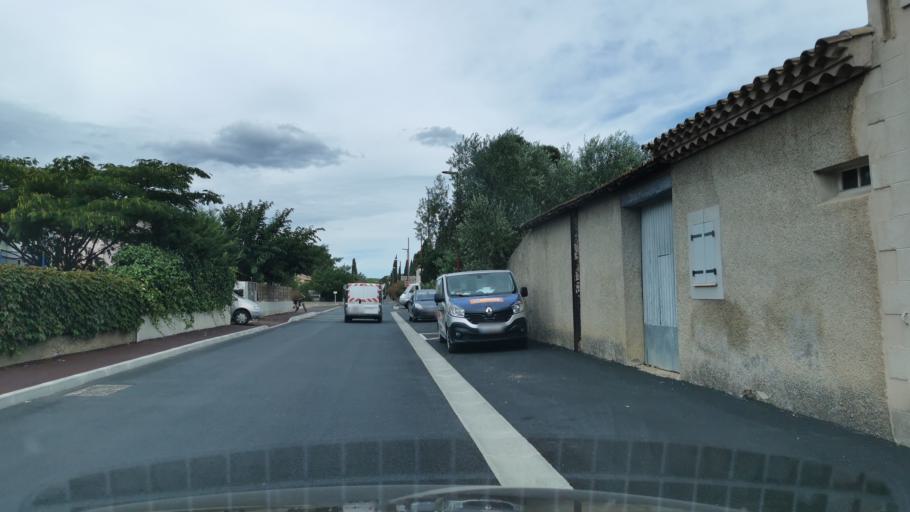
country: FR
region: Languedoc-Roussillon
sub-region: Departement de l'Aude
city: Saint-Marcel-sur-Aude
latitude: 43.2607
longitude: 2.9443
